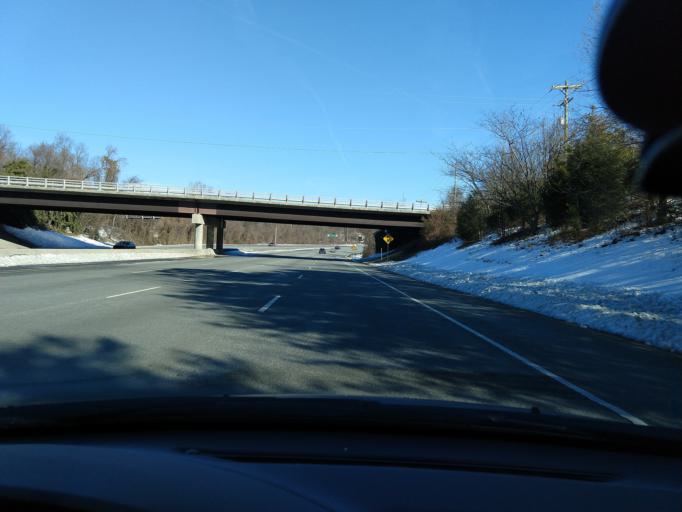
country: US
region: North Carolina
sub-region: Guilford County
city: Greensboro
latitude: 36.0398
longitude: -79.8178
